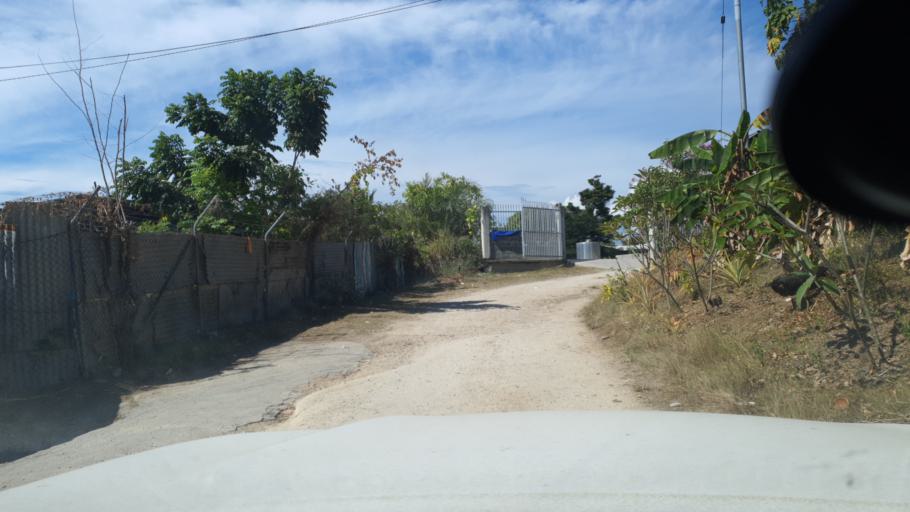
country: SB
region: Guadalcanal
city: Honiara
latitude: -9.4427
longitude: 159.9712
